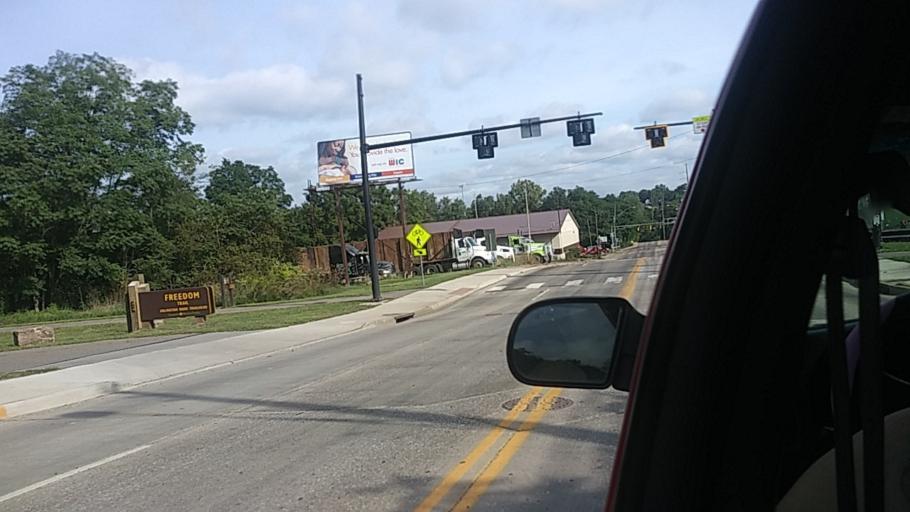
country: US
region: Ohio
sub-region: Summit County
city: Akron
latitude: 41.0837
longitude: -81.4904
